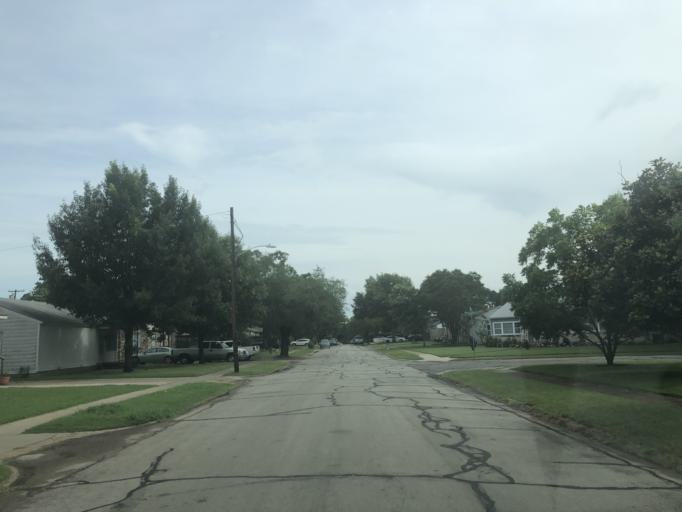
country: US
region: Texas
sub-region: Dallas County
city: Irving
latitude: 32.8024
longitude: -96.9518
